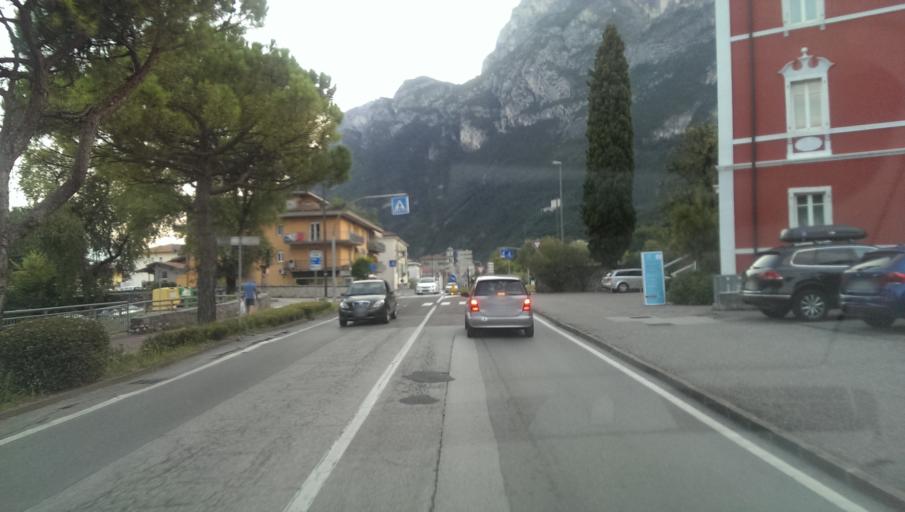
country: IT
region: Trentino-Alto Adige
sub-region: Provincia di Trento
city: Riva del Garda
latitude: 45.8926
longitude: 10.8471
